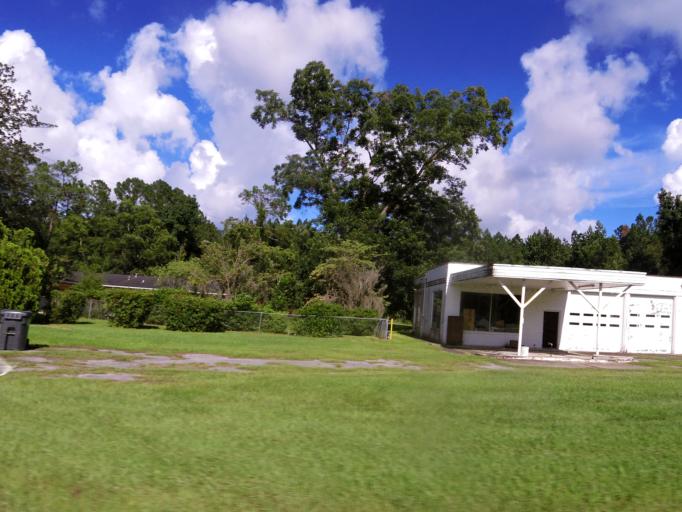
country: US
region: Georgia
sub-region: Camden County
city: Kingsland
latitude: 30.8714
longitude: -81.7045
